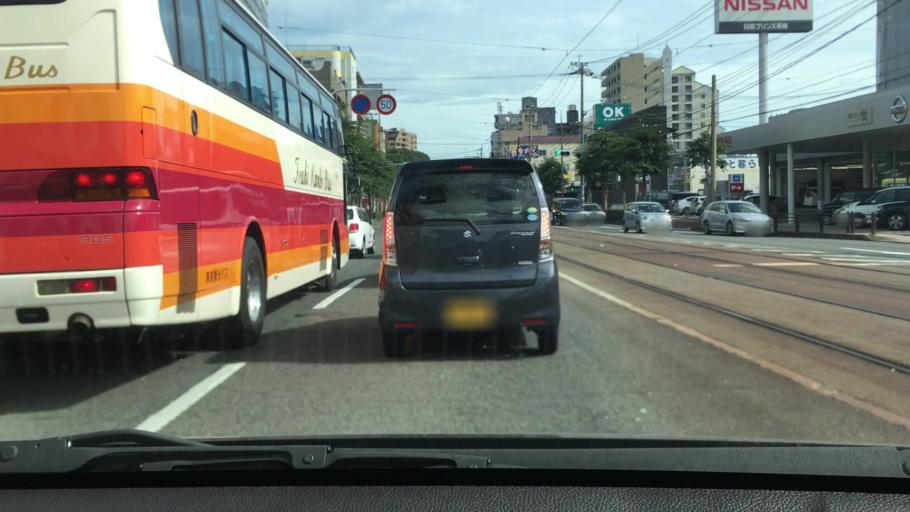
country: JP
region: Nagasaki
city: Obita
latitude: 32.7877
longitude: 129.8617
